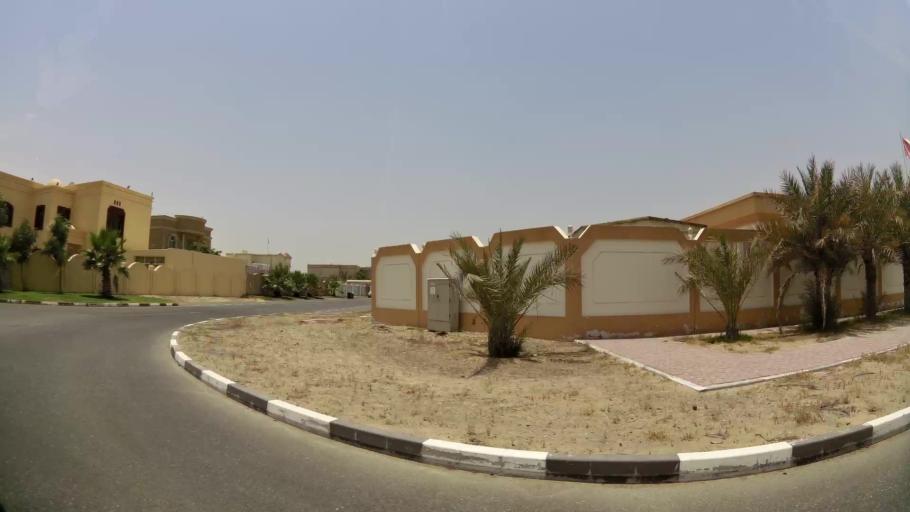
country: AE
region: Ash Shariqah
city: Sharjah
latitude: 25.2041
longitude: 55.3873
